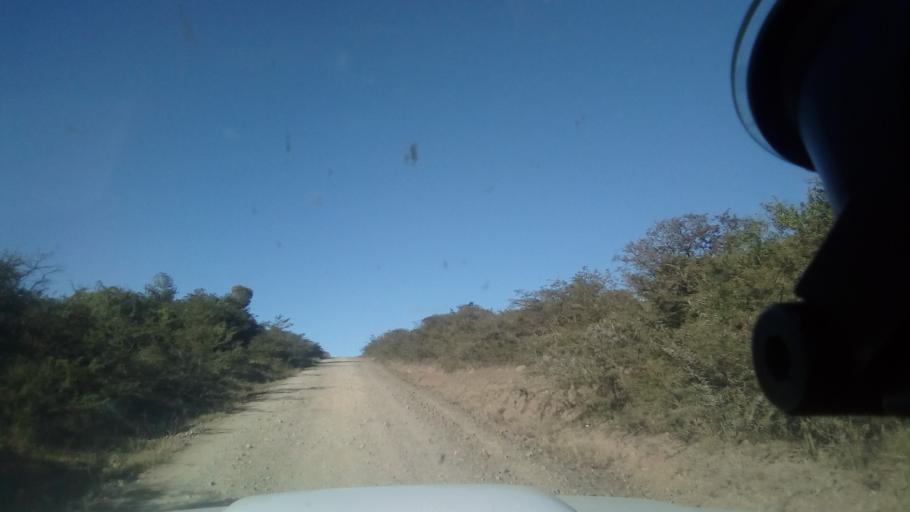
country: ZA
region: Eastern Cape
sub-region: Buffalo City Metropolitan Municipality
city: Bhisho
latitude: -32.7528
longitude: 27.3485
